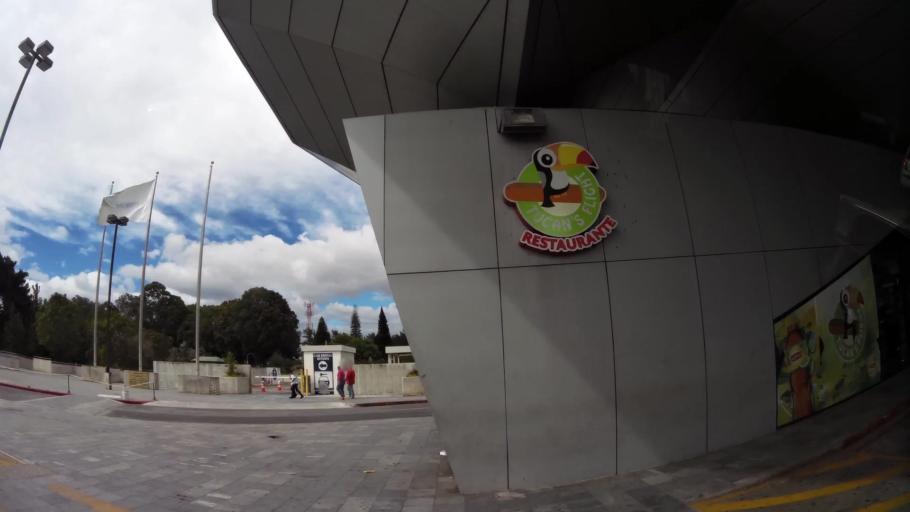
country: GT
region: Guatemala
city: Santa Catarina Pinula
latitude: 14.5881
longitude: -90.5309
